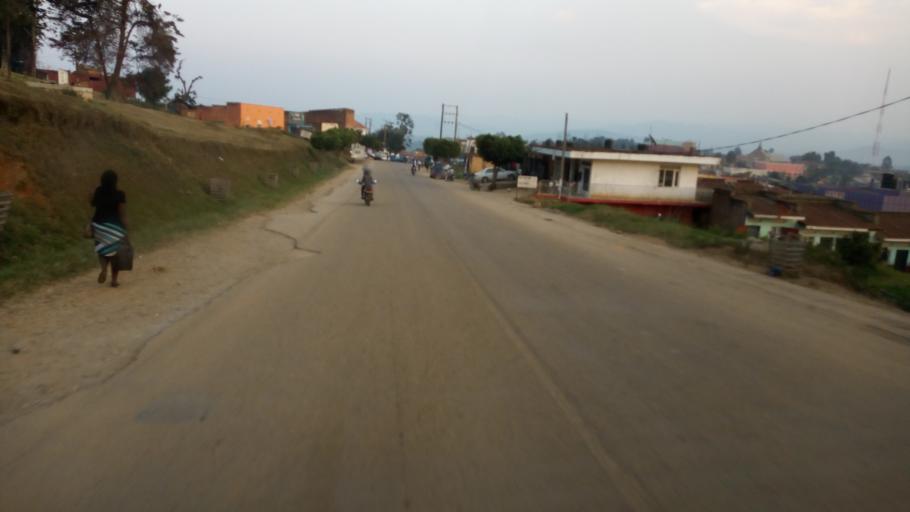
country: UG
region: Western Region
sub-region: Rukungiri District
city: Rukungiri
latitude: -0.7885
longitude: 29.9264
